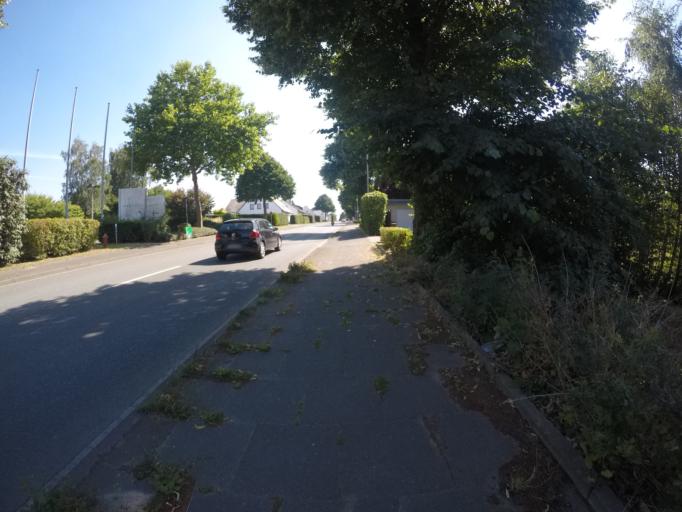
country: DE
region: North Rhine-Westphalia
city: Bad Oeynhausen
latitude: 52.1823
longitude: 8.7562
